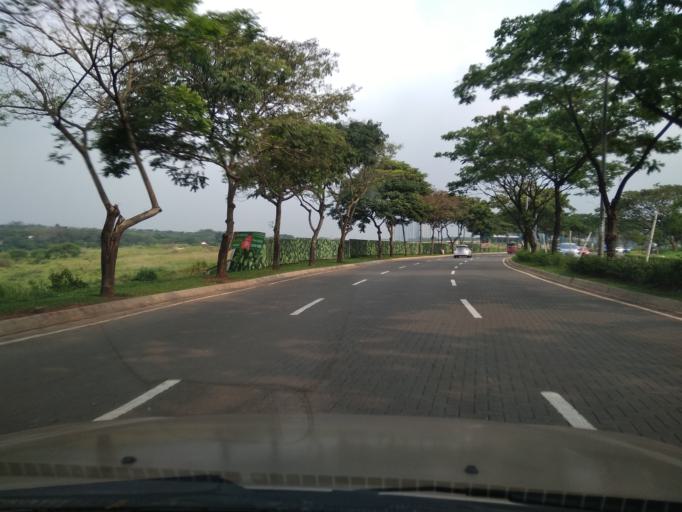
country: ID
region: West Java
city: Serpong
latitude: -6.2866
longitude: 106.6543
